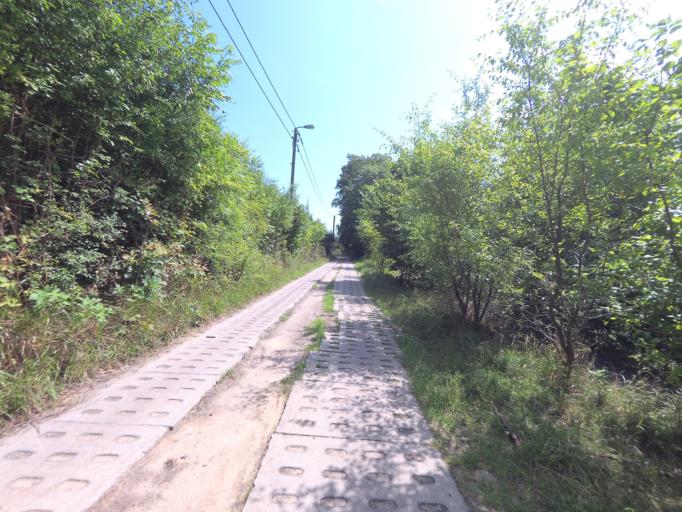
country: PL
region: Pomeranian Voivodeship
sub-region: Gdynia
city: Wielki Kack
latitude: 54.4873
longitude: 18.5063
